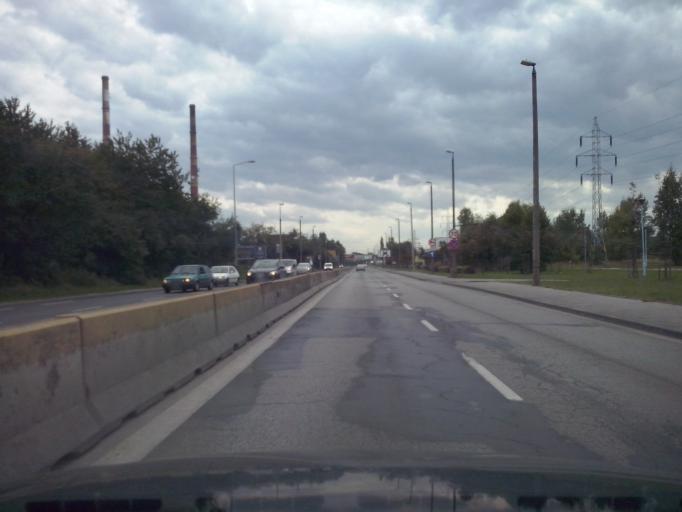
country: PL
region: Lesser Poland Voivodeship
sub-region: Krakow
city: Krakow
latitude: 50.0624
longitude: 20.0036
